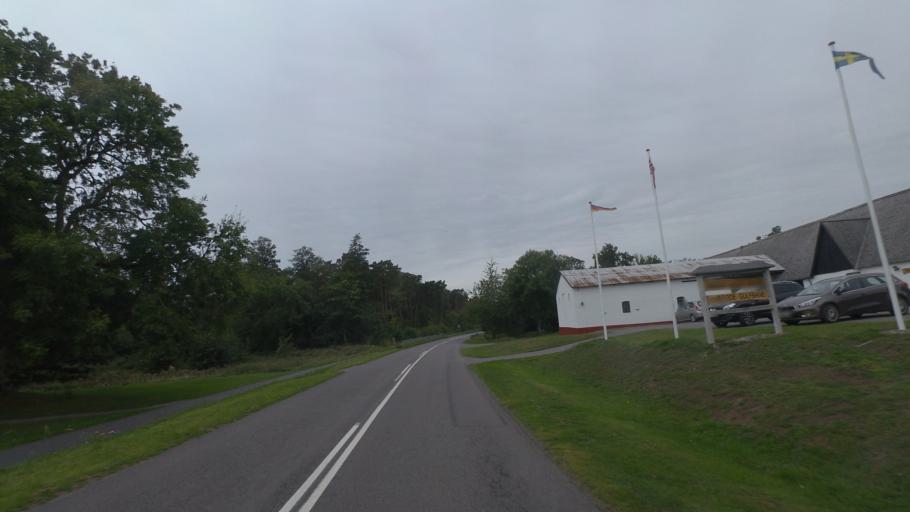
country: DK
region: Capital Region
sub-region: Bornholm Kommune
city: Nexo
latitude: 55.0030
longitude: 15.0304
